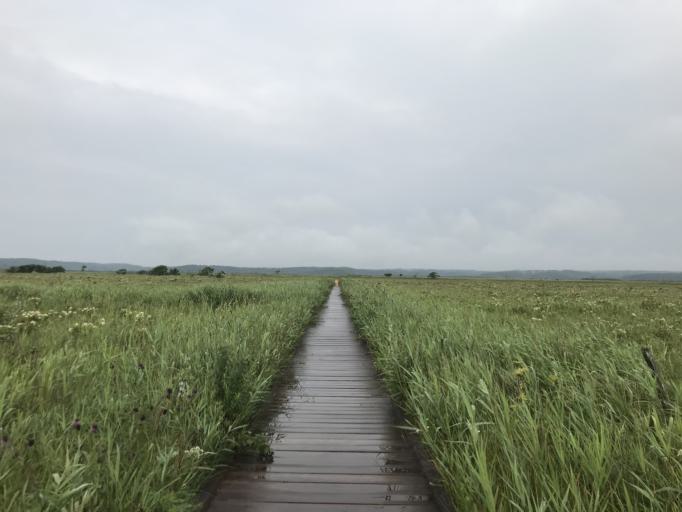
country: JP
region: Hokkaido
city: Nemuro
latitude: 43.0648
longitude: 145.0822
